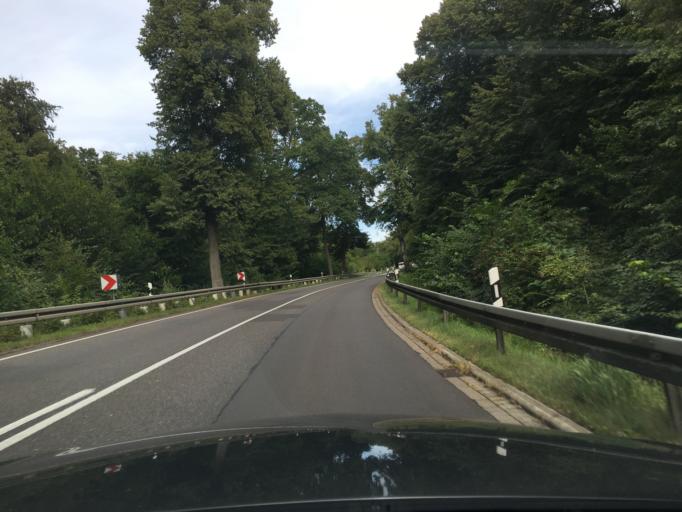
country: DE
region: Mecklenburg-Vorpommern
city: Wustrow
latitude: 53.4346
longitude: 13.1636
